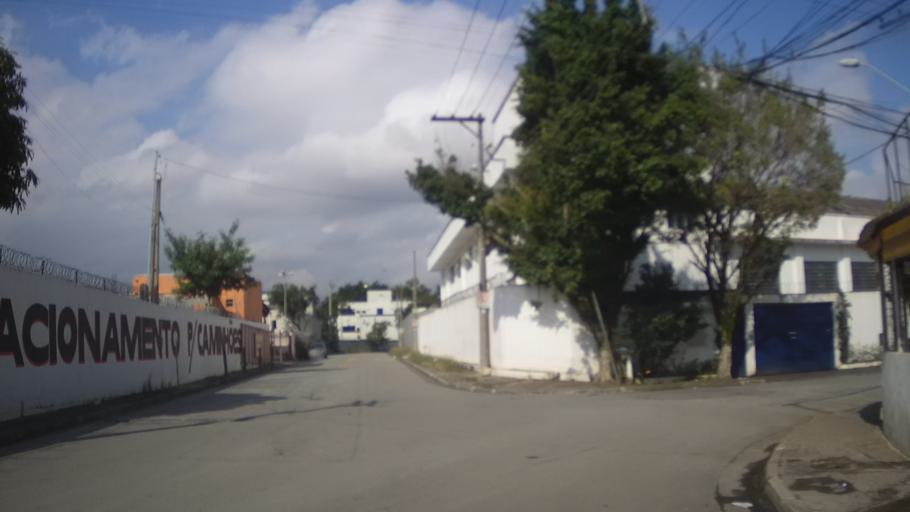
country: BR
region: Sao Paulo
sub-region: Guarulhos
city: Guarulhos
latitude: -23.4607
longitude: -46.4843
